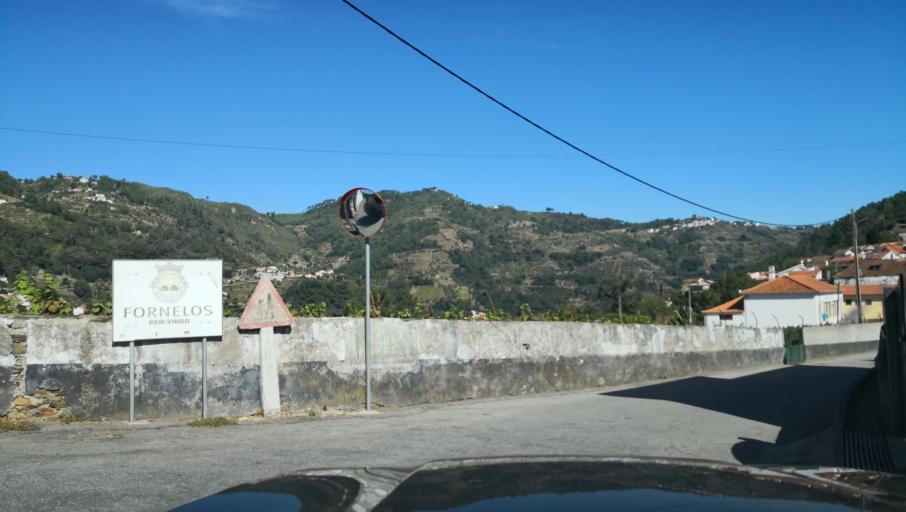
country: PT
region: Vila Real
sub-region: Santa Marta de Penaguiao
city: Santa Marta de Penaguiao
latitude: 41.2461
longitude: -7.8126
